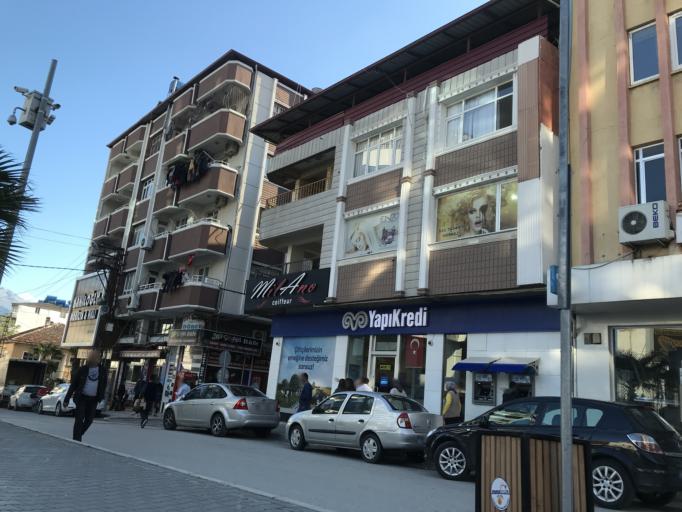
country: TR
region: Hatay
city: Samandag
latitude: 36.0832
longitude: 35.9807
